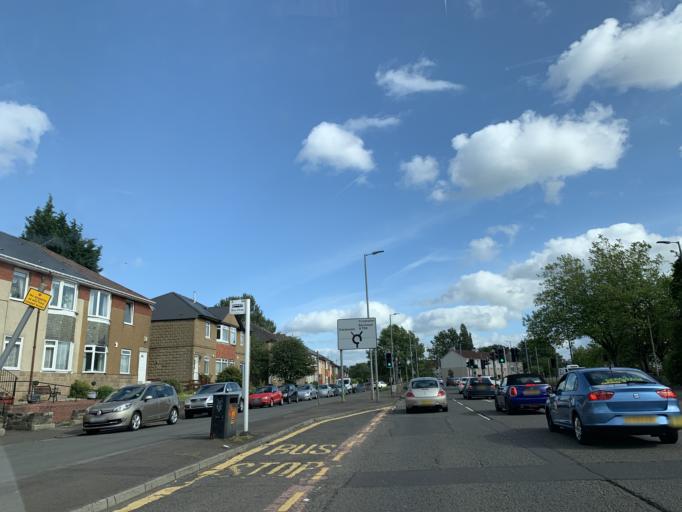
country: GB
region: Scotland
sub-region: Renfrewshire
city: Renfrew
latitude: 55.8528
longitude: -4.3639
